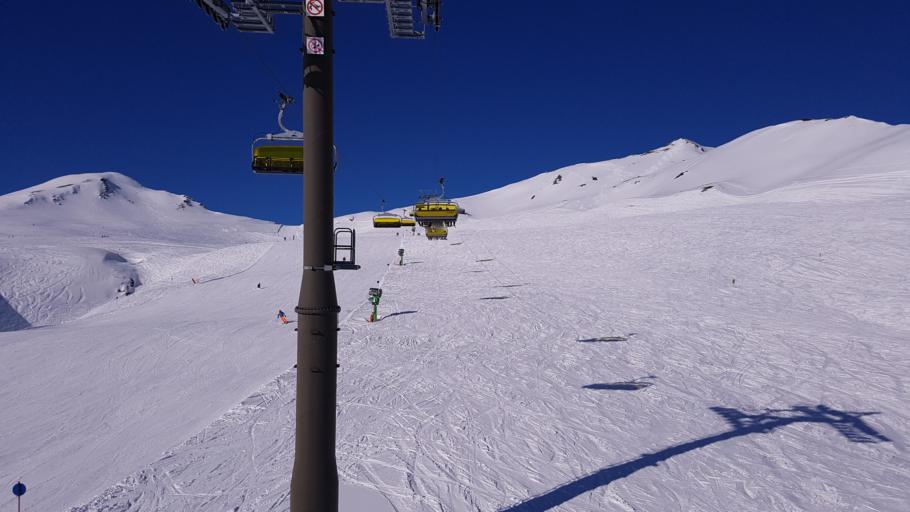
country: AT
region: Salzburg
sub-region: Politischer Bezirk Zell am See
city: Neukirchen am Grossvenediger
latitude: 47.2934
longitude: 12.2774
